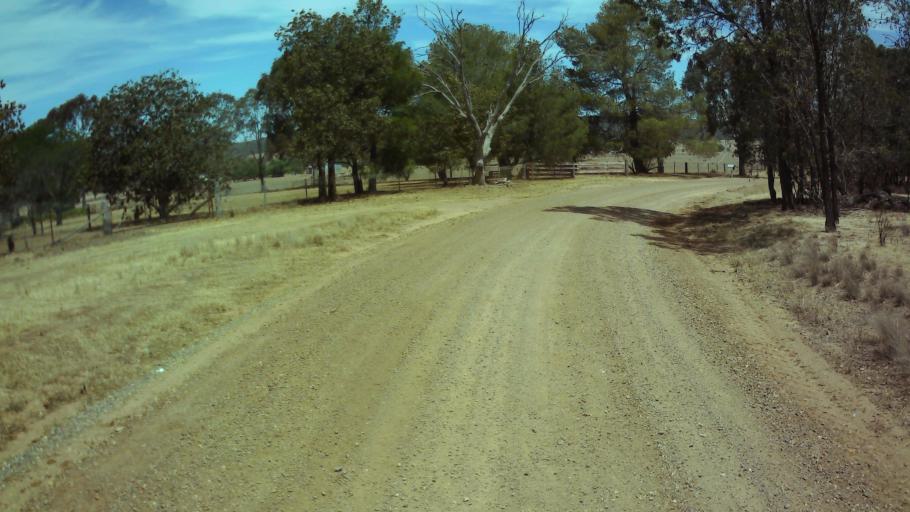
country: AU
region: New South Wales
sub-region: Weddin
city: Grenfell
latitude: -33.8298
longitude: 148.1754
